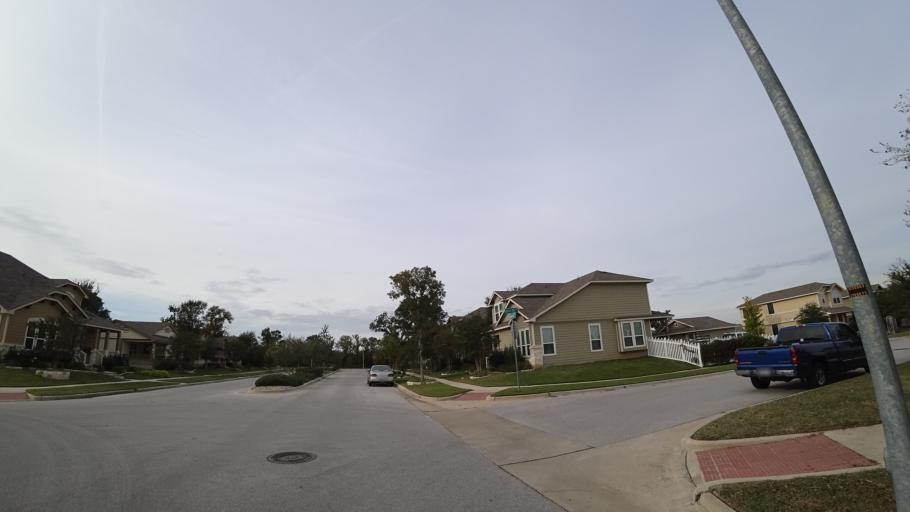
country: US
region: Texas
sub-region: Williamson County
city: Round Rock
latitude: 30.5095
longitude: -97.6595
